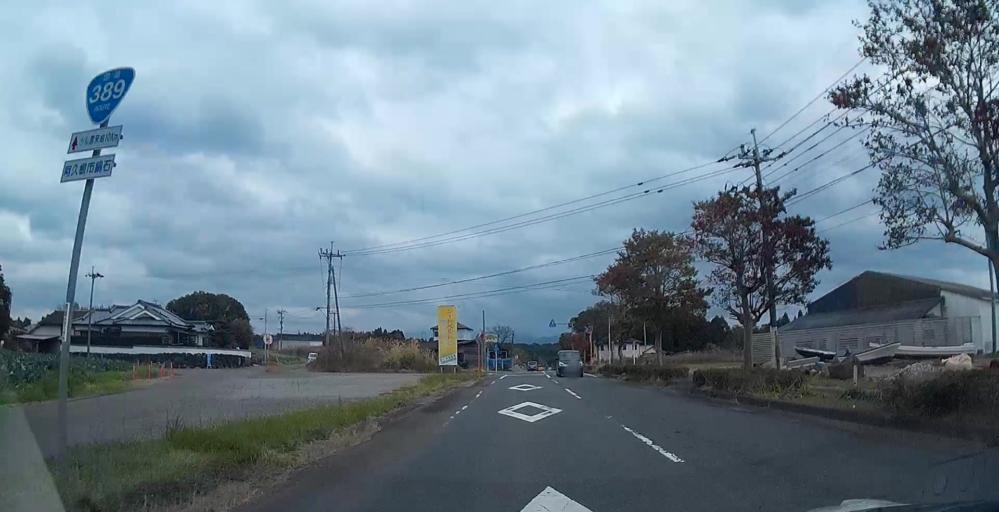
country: JP
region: Kagoshima
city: Akune
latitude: 32.0745
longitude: 130.2123
